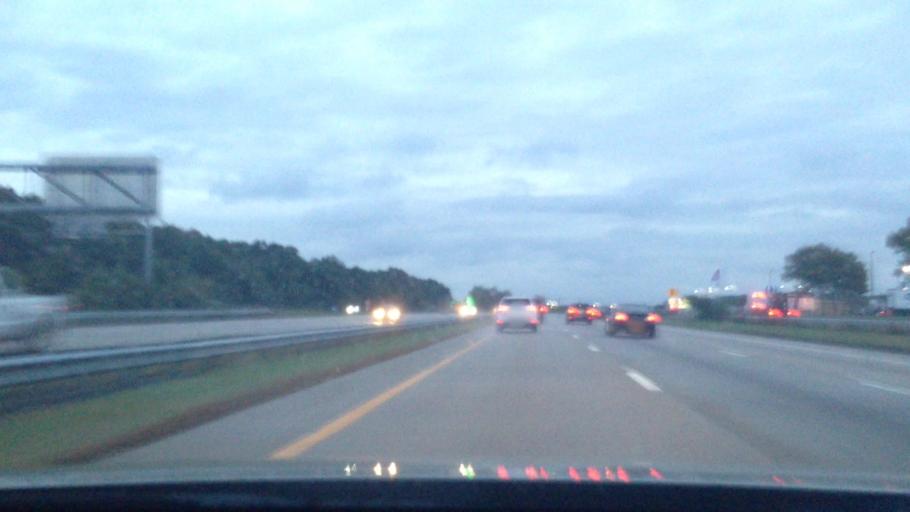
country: US
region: New York
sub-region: Suffolk County
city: Sayville
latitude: 40.7662
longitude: -73.0761
